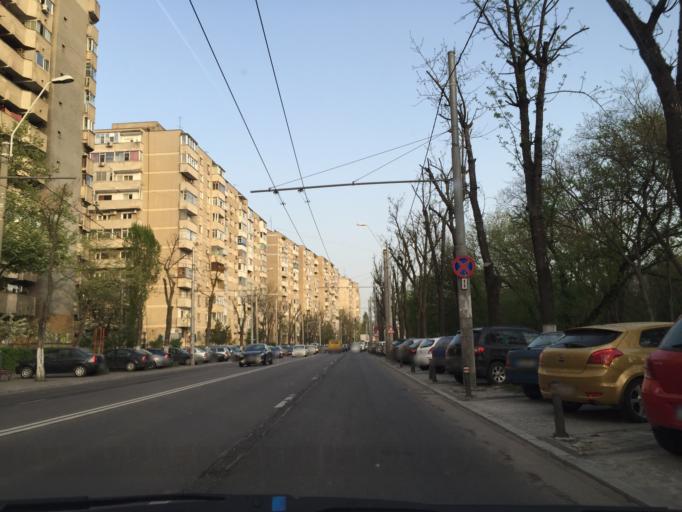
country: RO
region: Bucuresti
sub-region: Municipiul Bucuresti
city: Bucuresti
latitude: 44.4108
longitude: 26.1096
